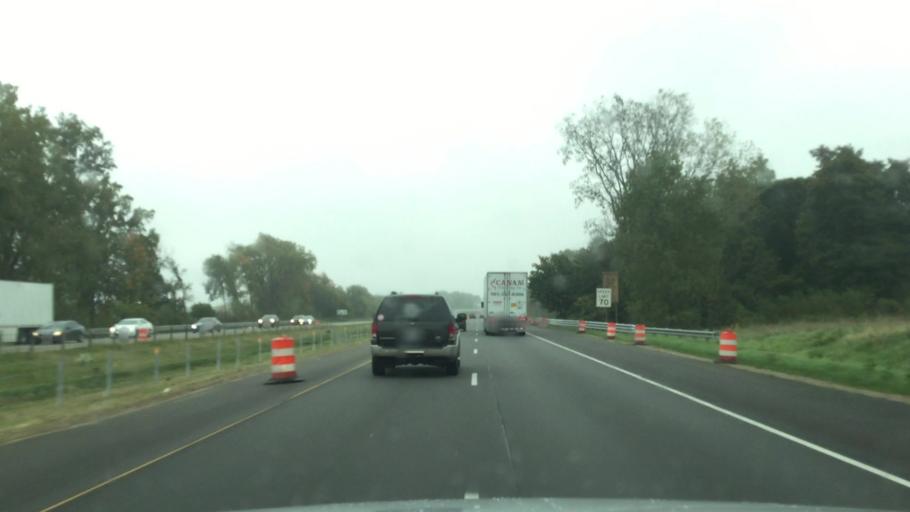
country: US
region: Michigan
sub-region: Van Buren County
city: Decatur
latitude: 42.1963
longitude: -86.0415
